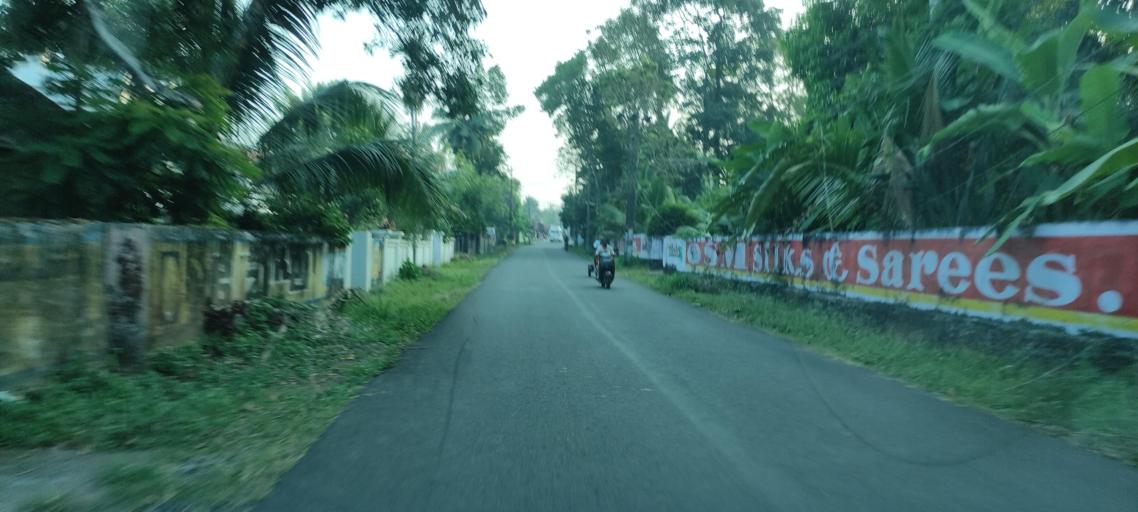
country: IN
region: Kerala
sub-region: Alappuzha
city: Kattanam
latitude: 9.1484
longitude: 76.5753
